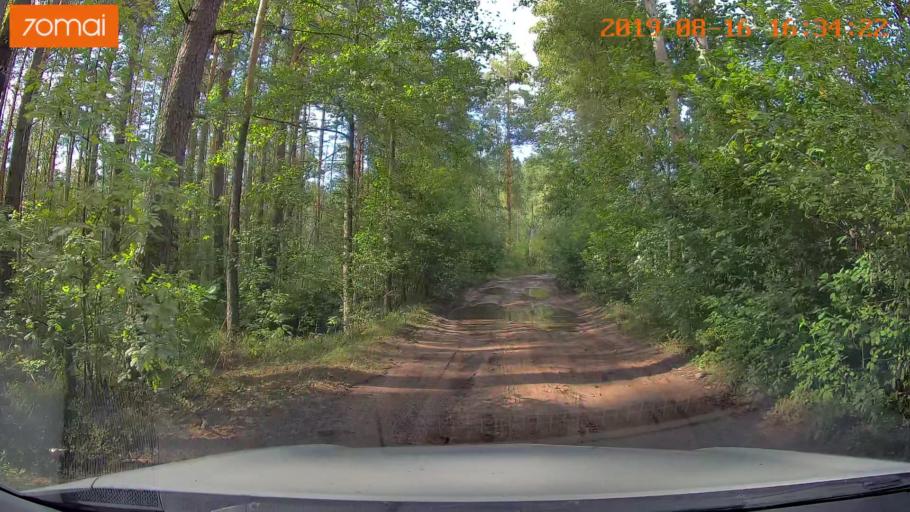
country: BY
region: Mogilev
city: Asipovichy
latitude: 53.2291
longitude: 28.7753
